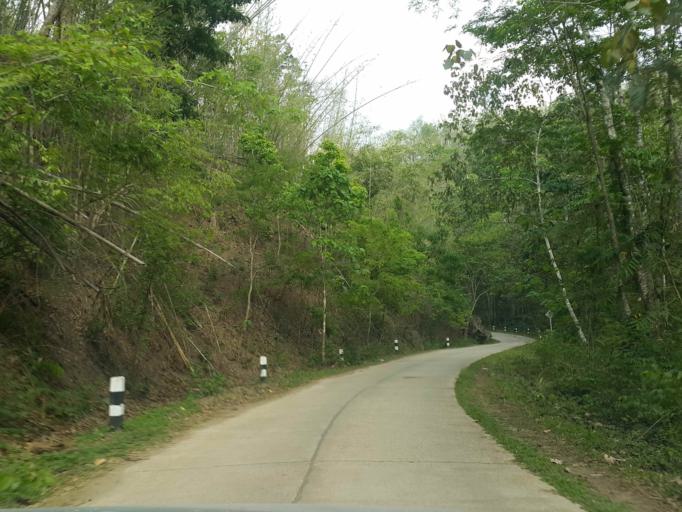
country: TH
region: Chiang Mai
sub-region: Amphoe Chiang Dao
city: Chiang Dao
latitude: 19.4109
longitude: 98.7902
